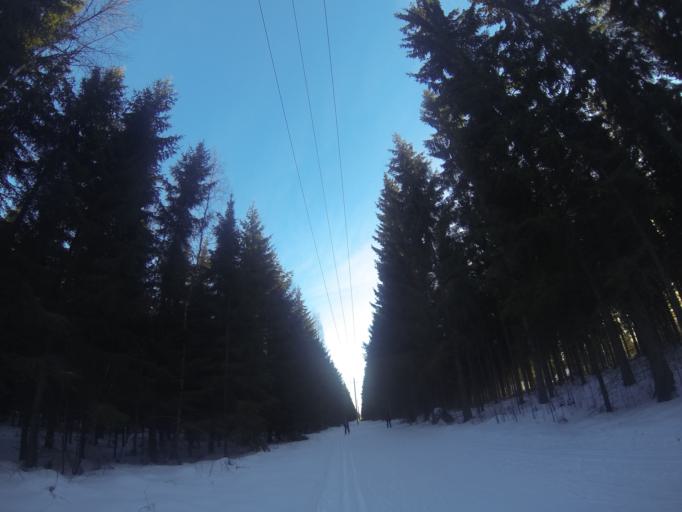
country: FI
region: Southern Savonia
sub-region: Savonlinna
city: Savonlinna
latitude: 61.9272
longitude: 28.8939
